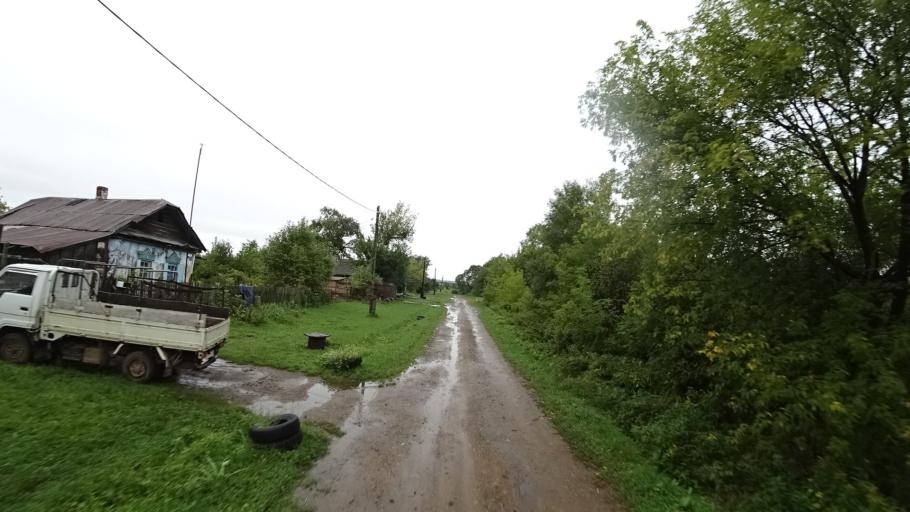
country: RU
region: Primorskiy
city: Monastyrishche
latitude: 44.2509
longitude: 132.4233
